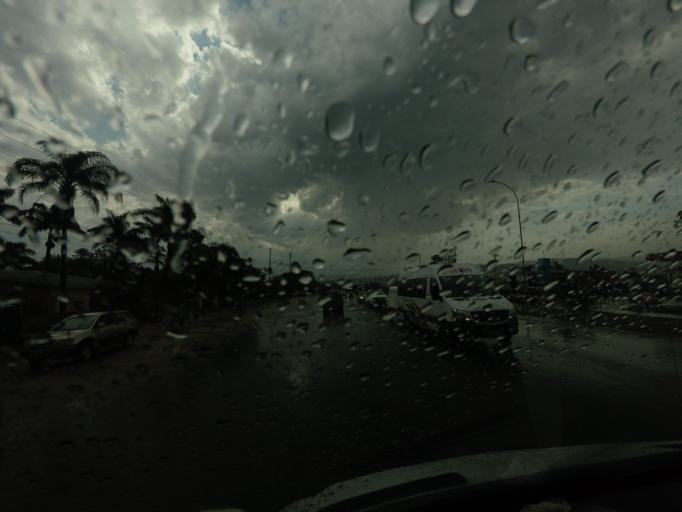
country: SZ
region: Manzini
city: Manzini
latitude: -26.4944
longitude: 31.4010
